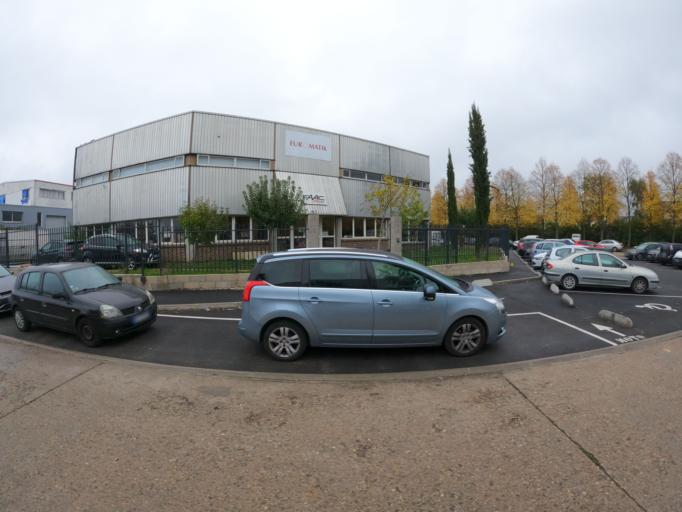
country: FR
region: Ile-de-France
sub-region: Departement du Val-de-Marne
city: Chennevieres-sur-Marne
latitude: 48.7952
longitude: 2.5467
